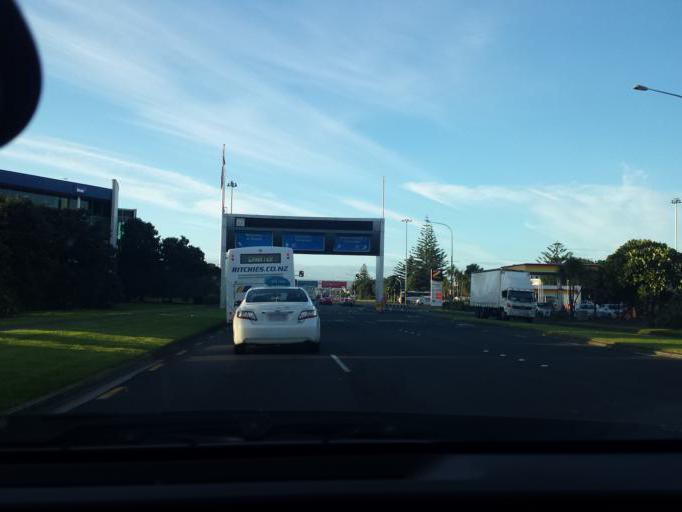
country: NZ
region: Auckland
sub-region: Auckland
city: Mangere
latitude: -37.0004
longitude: 174.7887
